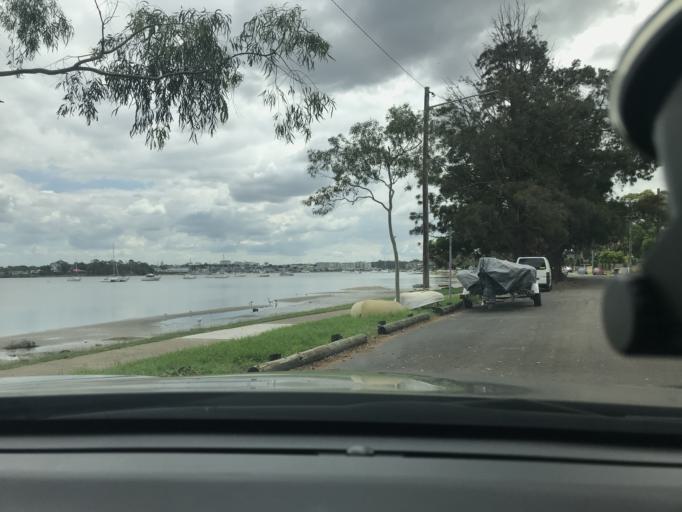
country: AU
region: New South Wales
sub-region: Canada Bay
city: Wareemba
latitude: -33.8579
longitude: 151.1281
